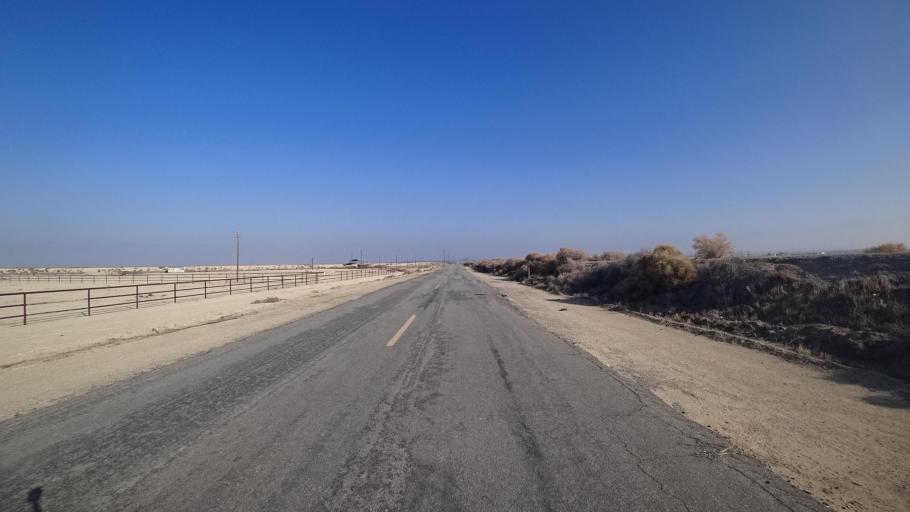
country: US
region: California
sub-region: Kern County
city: Maricopa
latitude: 35.1011
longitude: -119.3743
